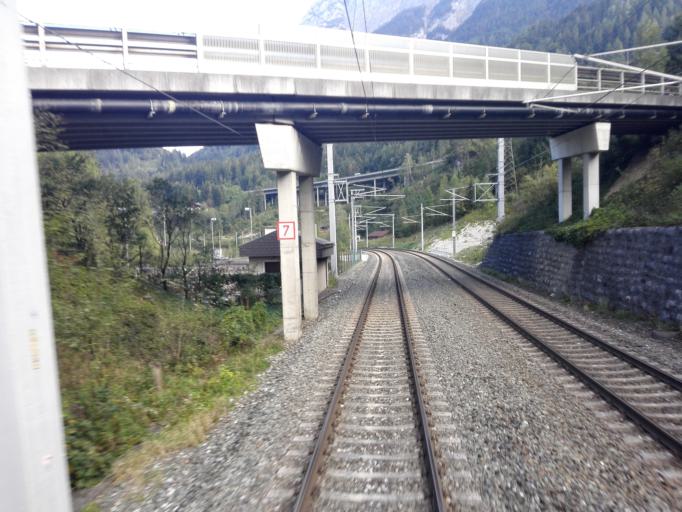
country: AT
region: Salzburg
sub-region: Politischer Bezirk Sankt Johann im Pongau
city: Werfen
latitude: 47.4822
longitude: 13.1926
